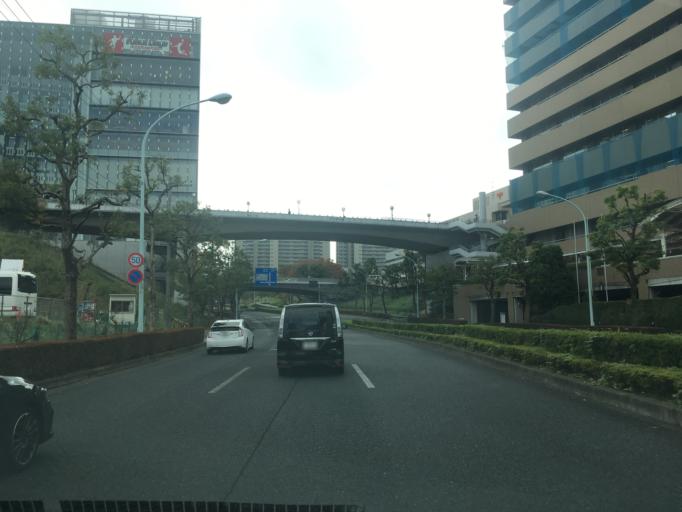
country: JP
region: Tokyo
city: Hino
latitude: 35.6230
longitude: 139.4227
